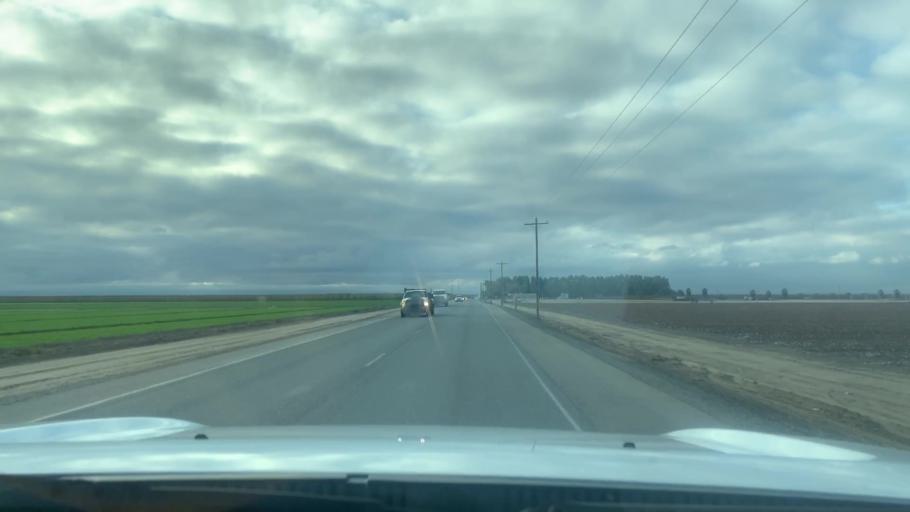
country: US
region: California
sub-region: Kern County
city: Buttonwillow
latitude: 35.5005
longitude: -119.4681
